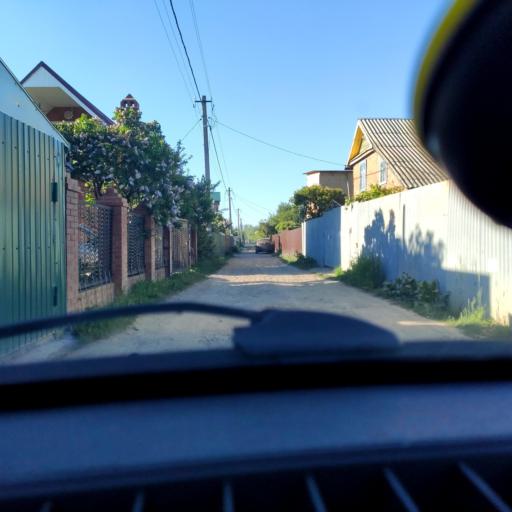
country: RU
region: Samara
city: Tol'yatti
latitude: 53.5932
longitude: 49.3144
